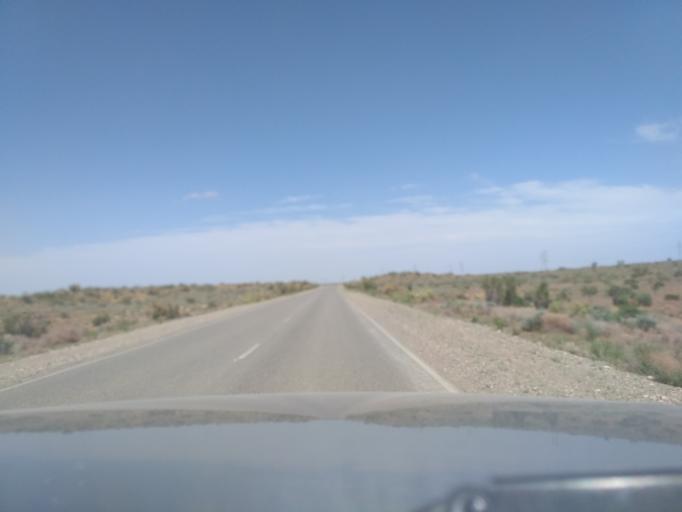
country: KZ
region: Ongtustik Qazaqstan
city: Sholaqqkorghan
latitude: 44.1240
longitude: 68.8854
